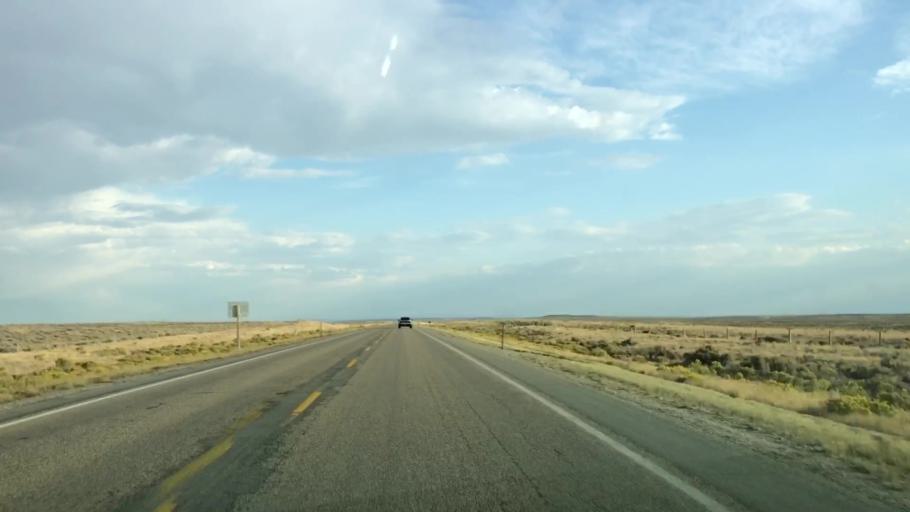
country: US
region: Wyoming
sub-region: Sublette County
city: Pinedale
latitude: 42.4075
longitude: -109.5505
